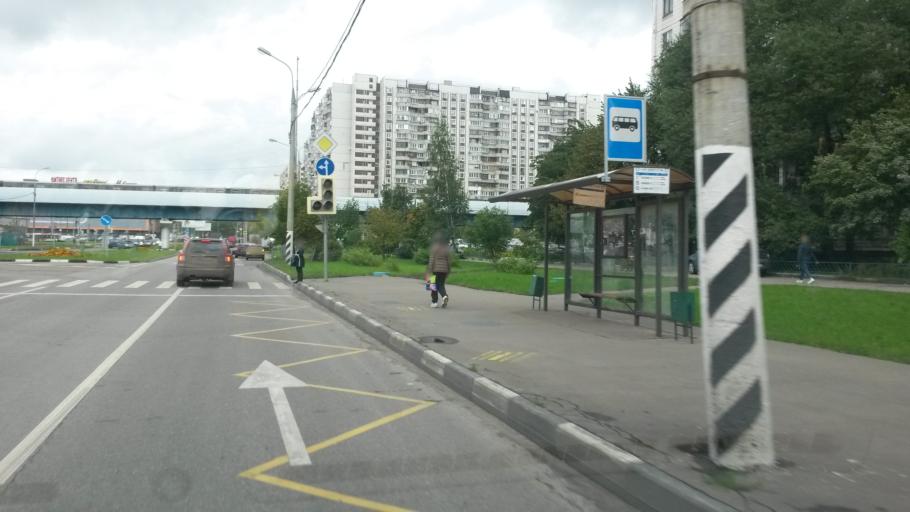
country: RU
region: Moskovskaya
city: Shcherbinka
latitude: 55.5448
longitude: 37.5472
